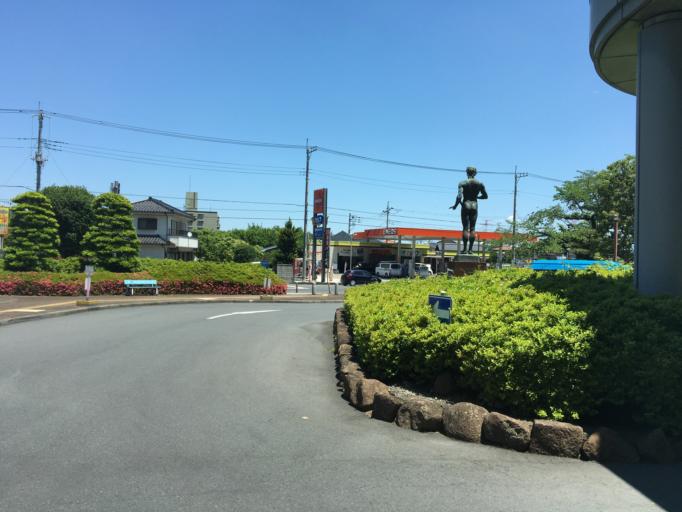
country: JP
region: Saitama
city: Sakado
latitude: 35.9348
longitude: 139.3934
